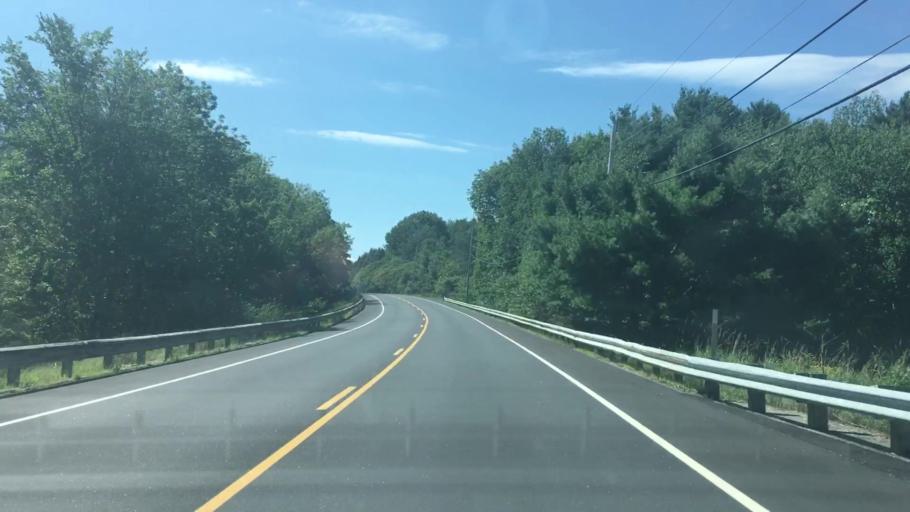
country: US
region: Maine
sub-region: Kennebec County
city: Monmouth
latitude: 44.1892
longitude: -69.9425
